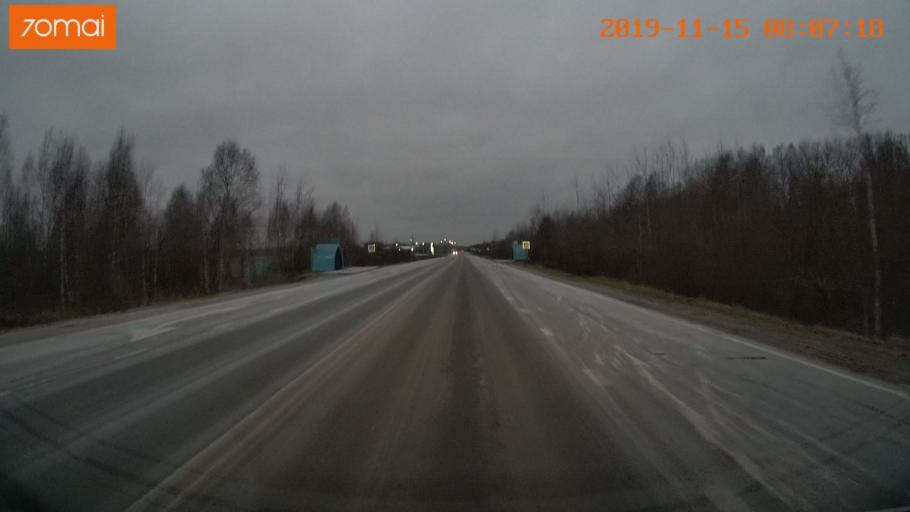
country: RU
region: Vologda
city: Cherepovets
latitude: 59.0258
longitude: 38.0197
